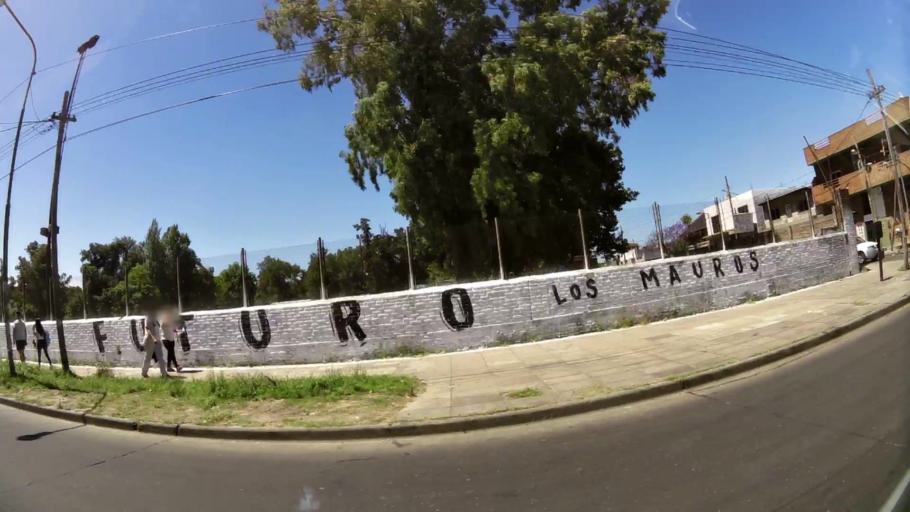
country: AR
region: Buenos Aires
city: Caseros
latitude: -34.5805
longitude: -58.5600
